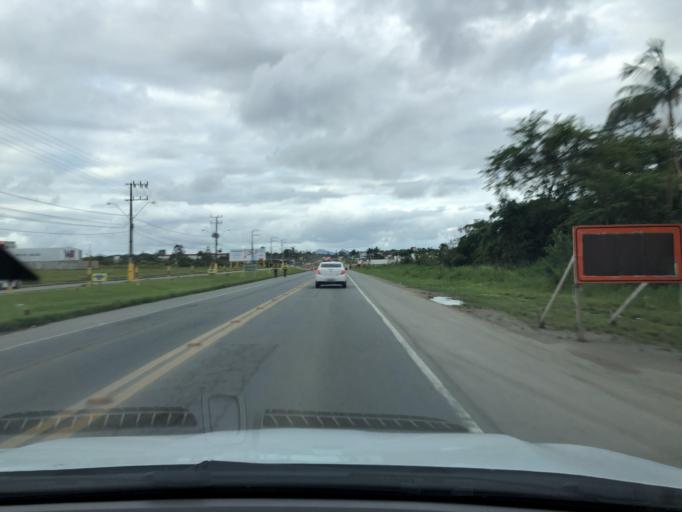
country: BR
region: Santa Catarina
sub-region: Joinville
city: Joinville
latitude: -26.4041
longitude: -48.7453
